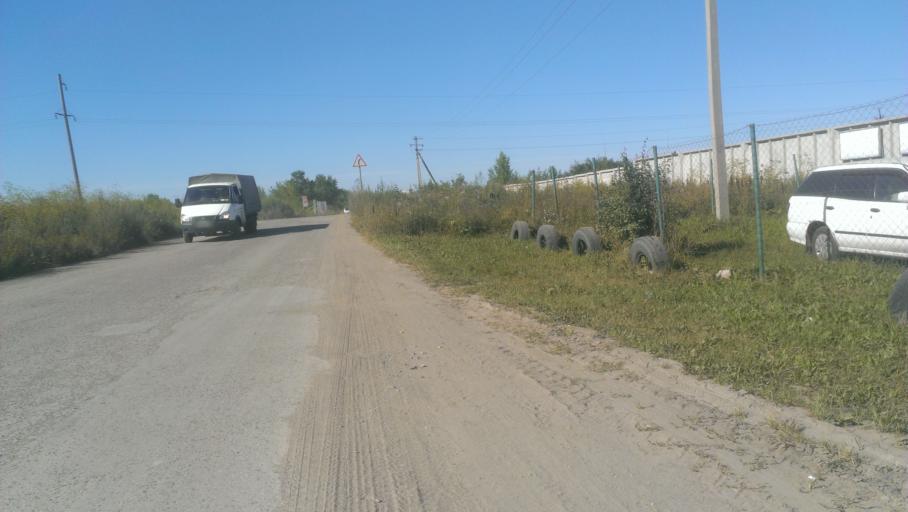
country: RU
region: Altai Krai
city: Novosilikatnyy
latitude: 53.3354
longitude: 83.6352
